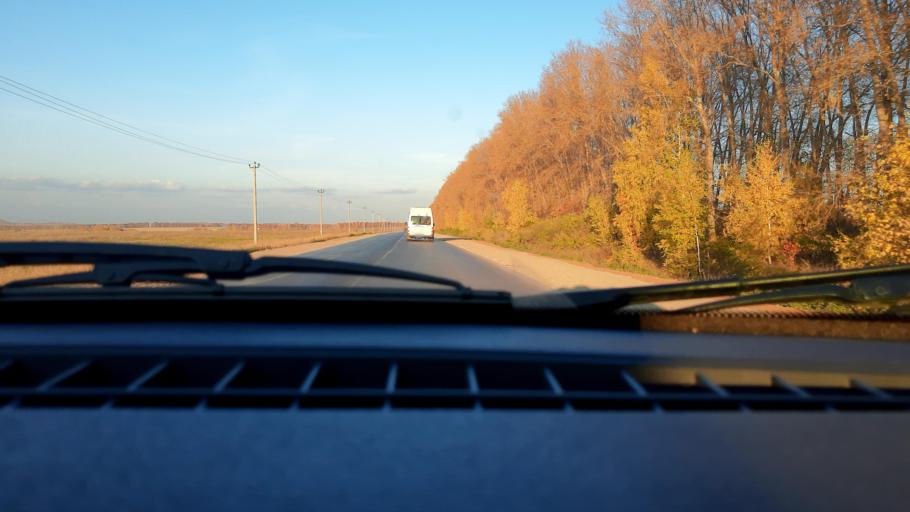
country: RU
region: Bashkortostan
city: Asanovo
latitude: 54.8183
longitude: 55.6046
